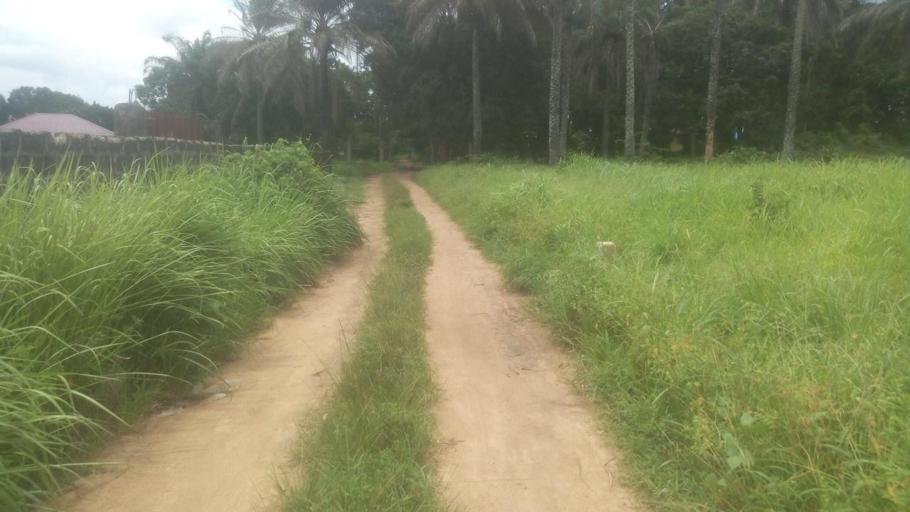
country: SL
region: Northern Province
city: Masoyila
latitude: 8.5568
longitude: -13.1658
